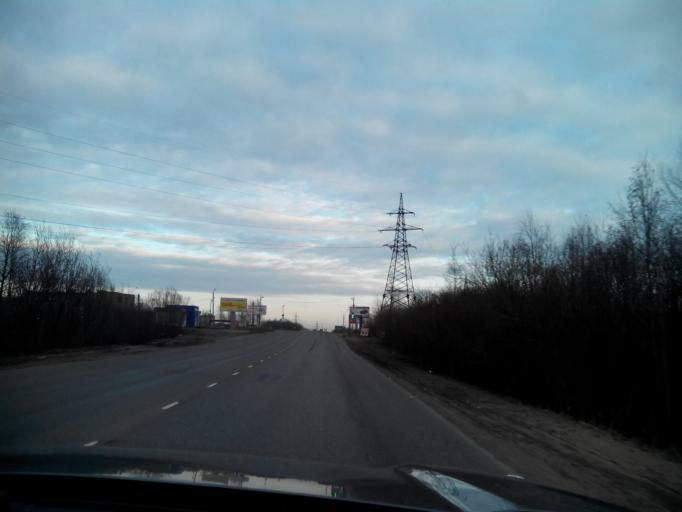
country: RU
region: Arkhangelskaya
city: Arkhangel'sk
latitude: 64.5203
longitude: 40.6741
